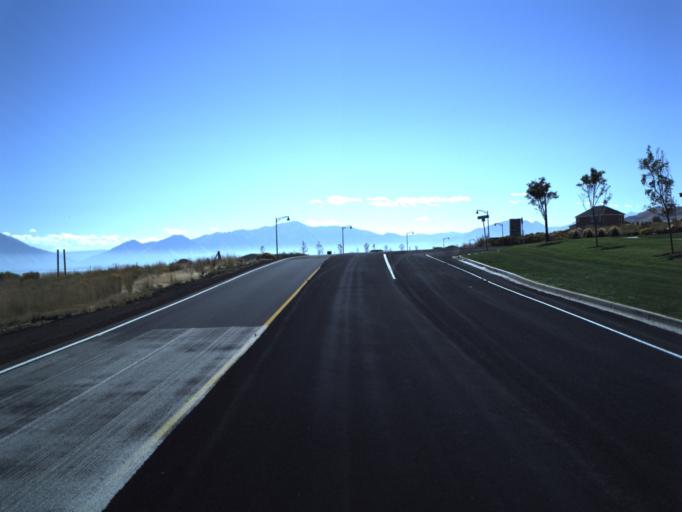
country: US
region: Utah
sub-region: Utah County
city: Saratoga Springs
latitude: 40.3055
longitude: -111.8868
